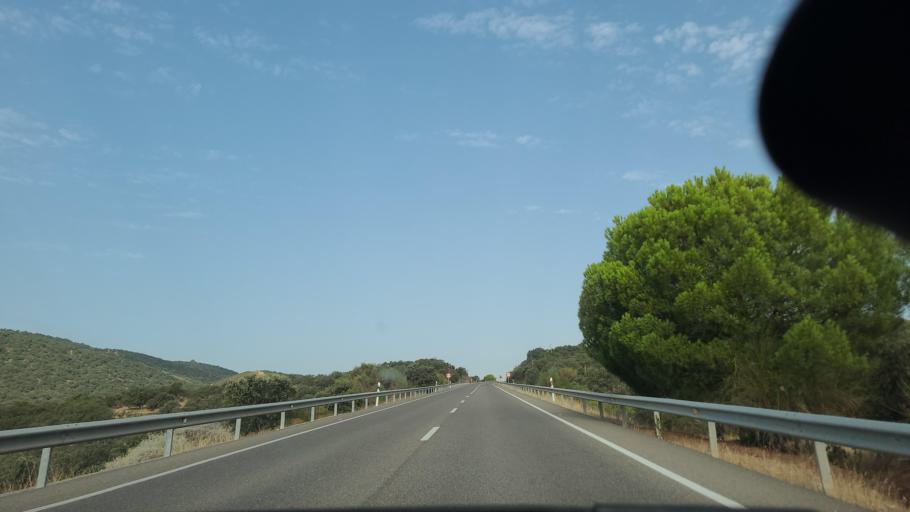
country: ES
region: Andalusia
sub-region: Province of Cordoba
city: Espiel
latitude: 38.1901
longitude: -5.0892
